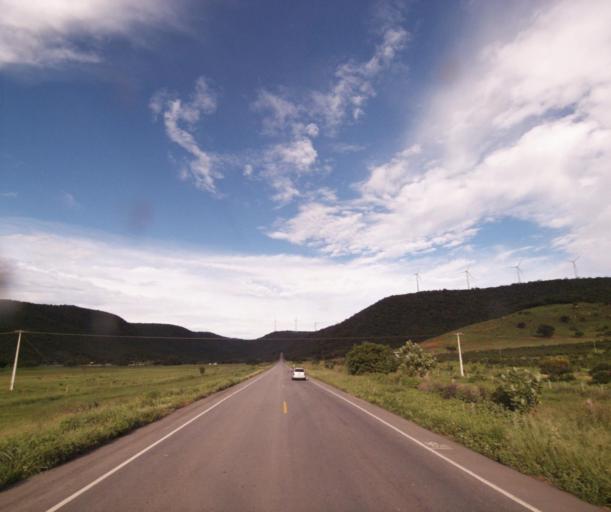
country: BR
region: Bahia
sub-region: Guanambi
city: Guanambi
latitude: -14.1591
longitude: -42.7109
